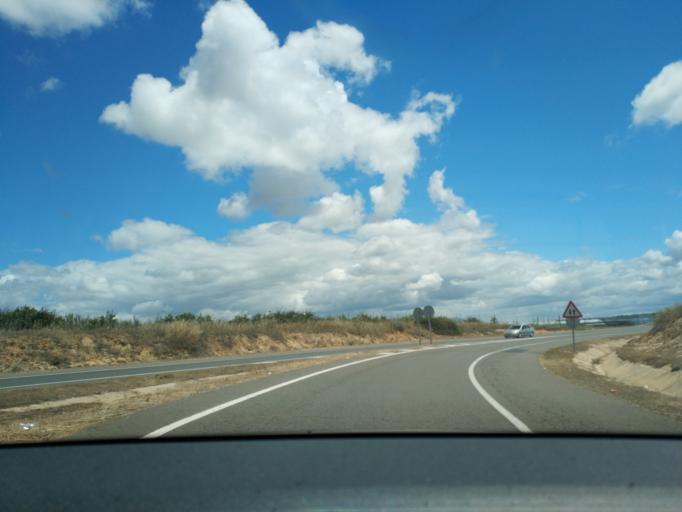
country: ES
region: Andalusia
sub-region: Provincia de Huelva
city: Aljaraque
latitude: 37.3246
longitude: -7.0750
